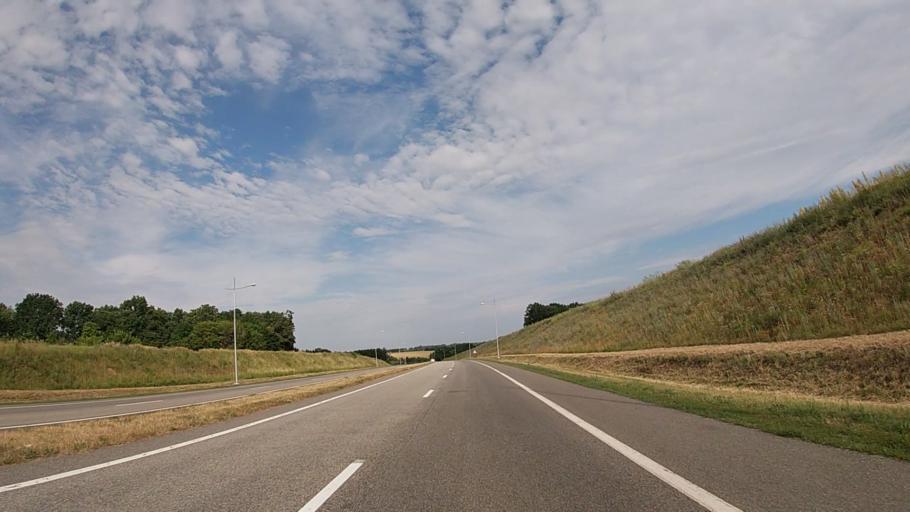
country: RU
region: Belgorod
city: Tomarovka
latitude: 50.7063
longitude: 36.2136
